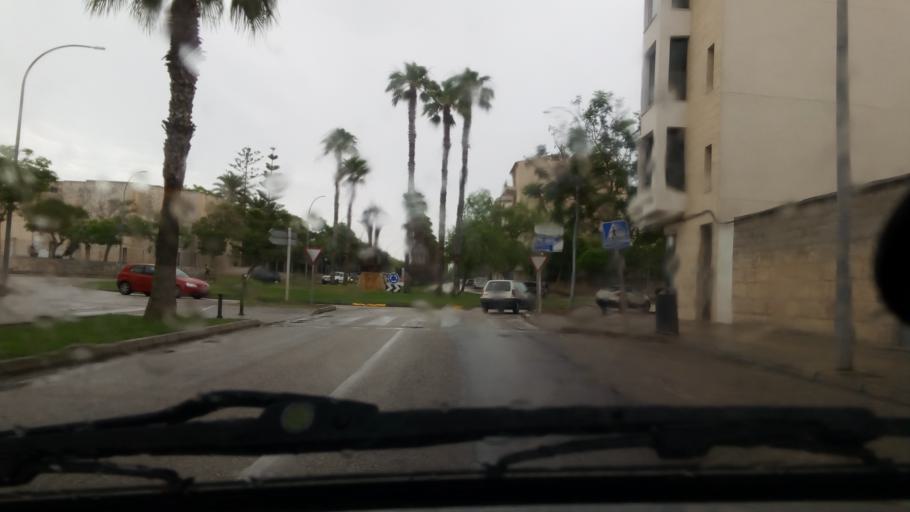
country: ES
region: Balearic Islands
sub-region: Illes Balears
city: Manacor
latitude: 39.5705
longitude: 3.2187
